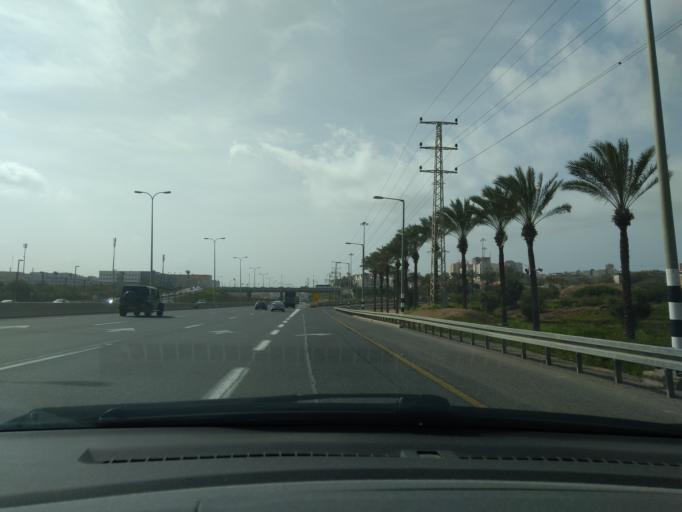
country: IL
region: Central District
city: Even Yehuda
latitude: 32.2902
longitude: 34.8601
